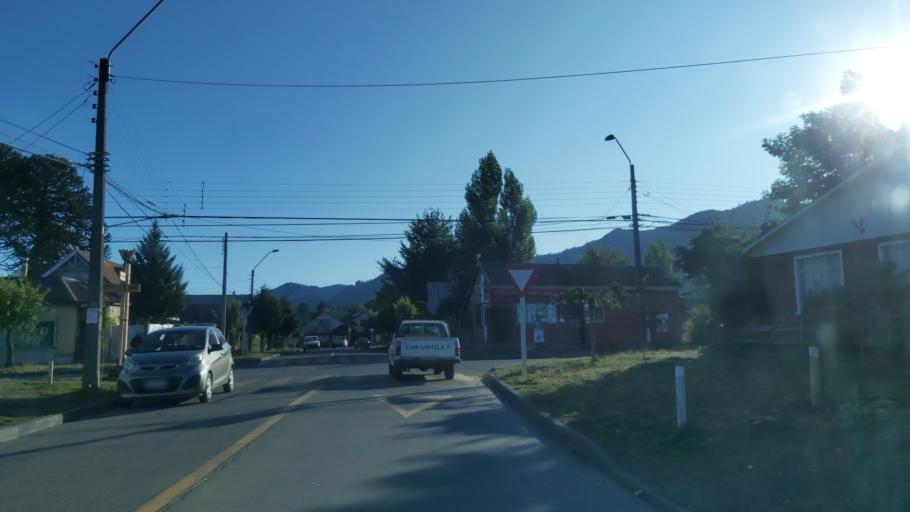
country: AR
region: Neuquen
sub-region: Departamento de Loncopue
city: Loncopue
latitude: -38.4503
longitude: -71.3712
